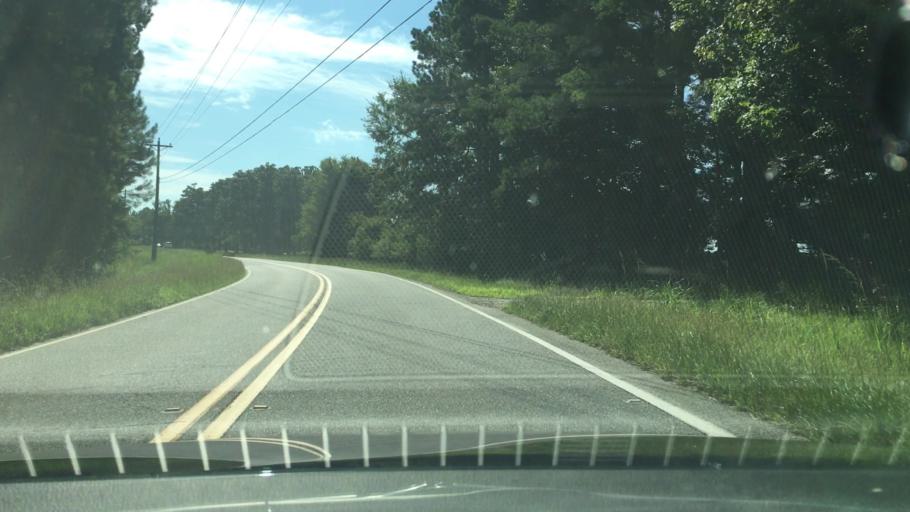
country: US
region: Georgia
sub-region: Putnam County
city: Jefferson
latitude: 33.4437
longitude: -83.2904
